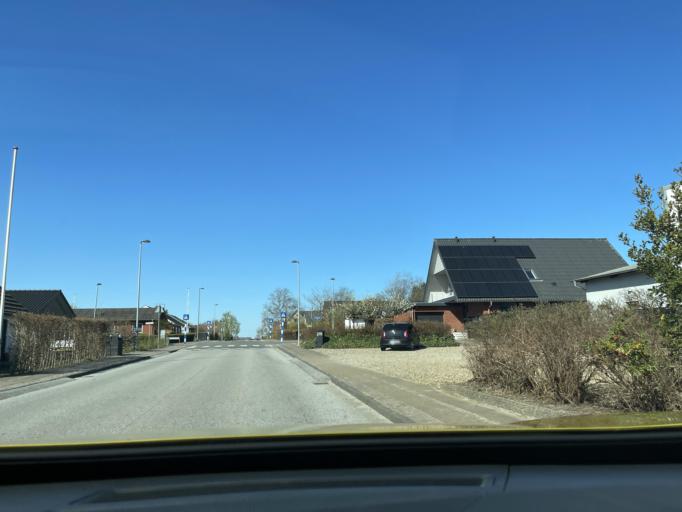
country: DK
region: Central Jutland
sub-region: Ikast-Brande Kommune
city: Bording Kirkeby
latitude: 56.1418
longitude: 9.2742
